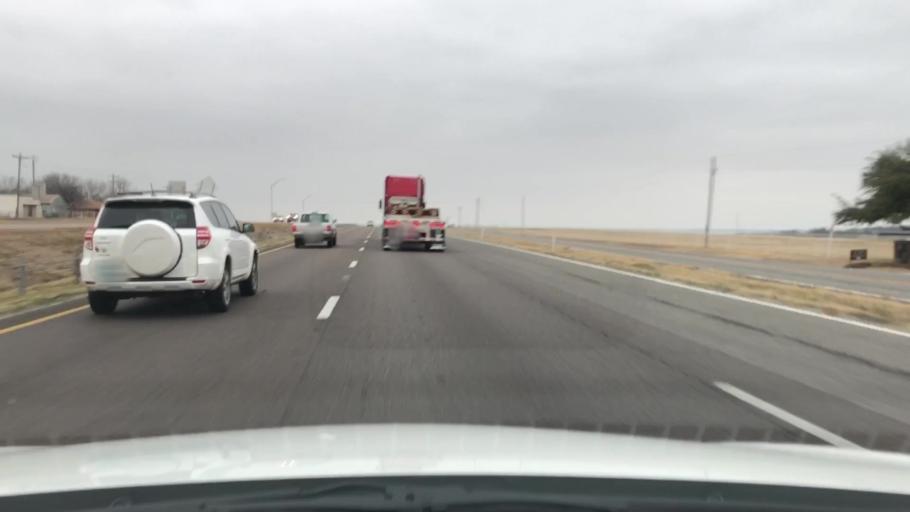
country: US
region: Texas
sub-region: Cooke County
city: Gainesville
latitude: 33.6863
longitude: -97.1588
